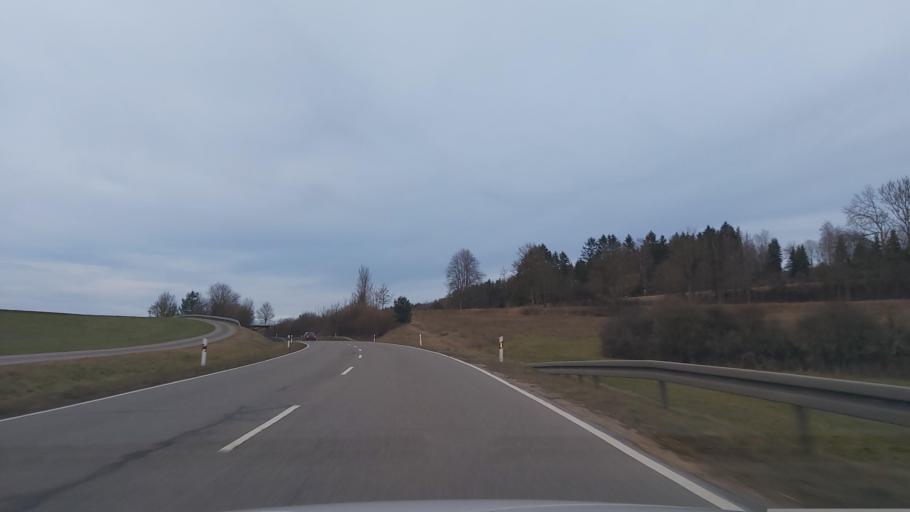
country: DE
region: Baden-Wuerttemberg
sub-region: Tuebingen Region
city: Munsingen
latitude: 48.4198
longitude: 9.4745
